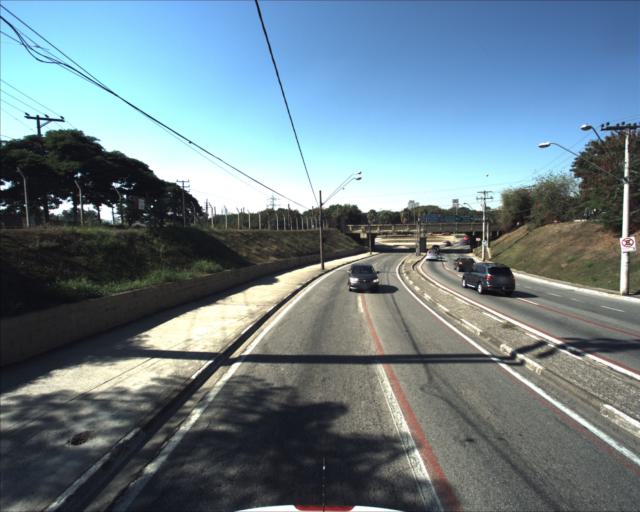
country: BR
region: Sao Paulo
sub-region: Sorocaba
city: Sorocaba
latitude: -23.4969
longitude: -47.4526
